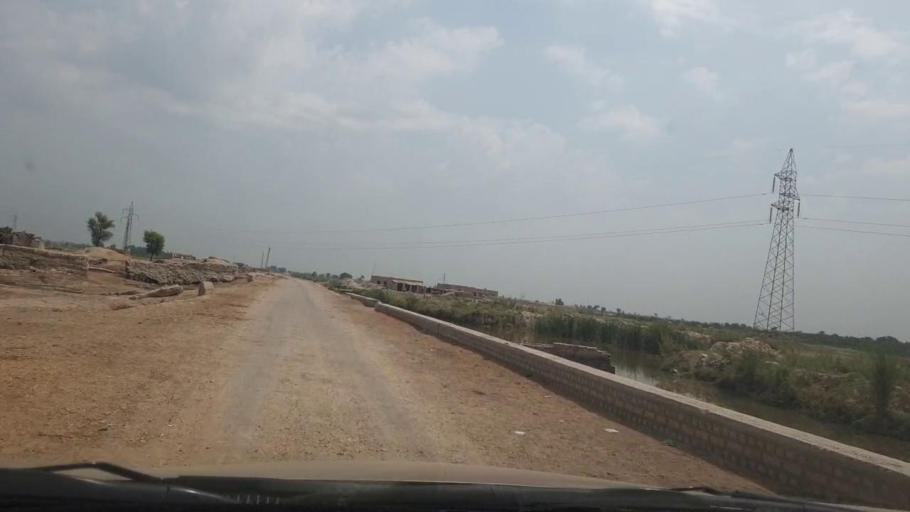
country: PK
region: Sindh
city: Ratodero
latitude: 27.7055
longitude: 68.2691
